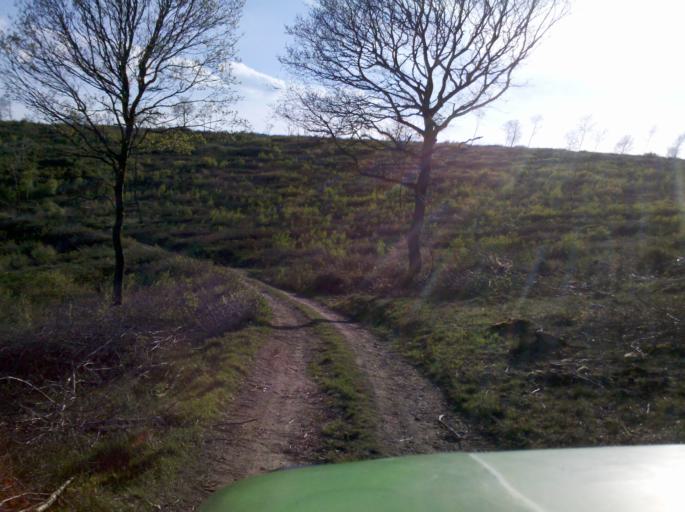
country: DE
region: Hesse
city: Dillenburg
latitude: 50.8075
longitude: 8.2508
